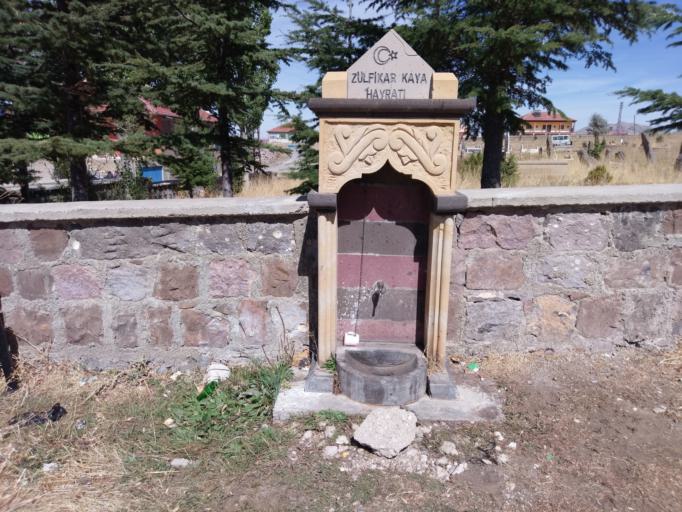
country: TR
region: Kayseri
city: Toklar
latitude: 38.4074
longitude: 36.0837
